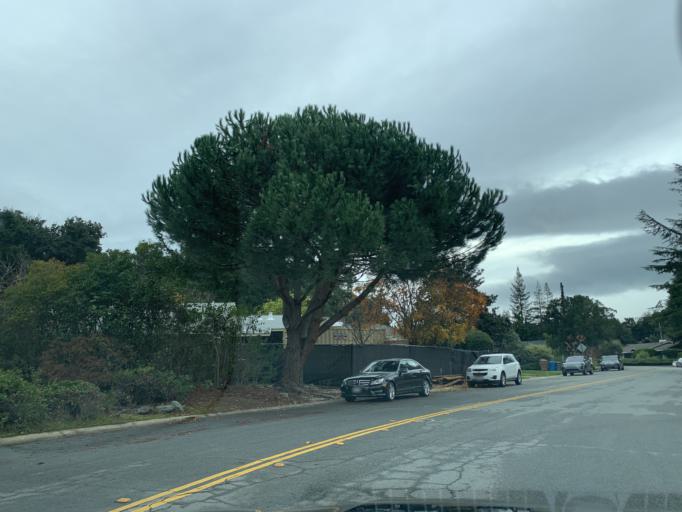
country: US
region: California
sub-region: Santa Clara County
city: Cupertino
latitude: 37.3292
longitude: -122.0607
